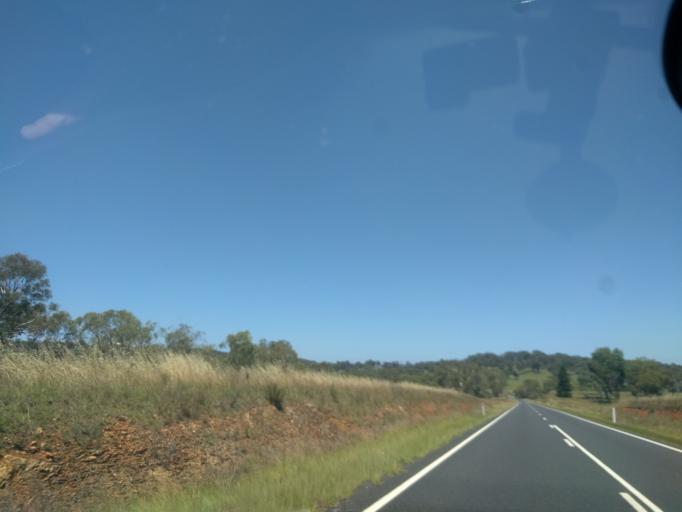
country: AU
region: New South Wales
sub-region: Armidale Dumaresq
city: Armidale
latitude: -30.5346
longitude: 151.7245
